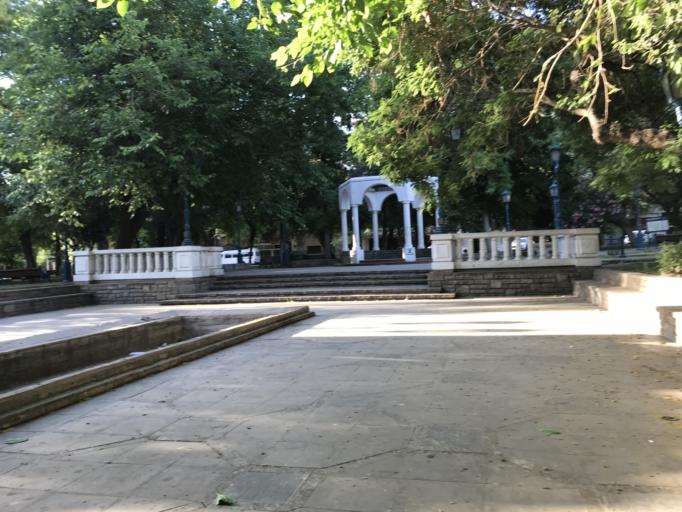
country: AR
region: Mendoza
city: Mendoza
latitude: -32.8900
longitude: -68.8455
